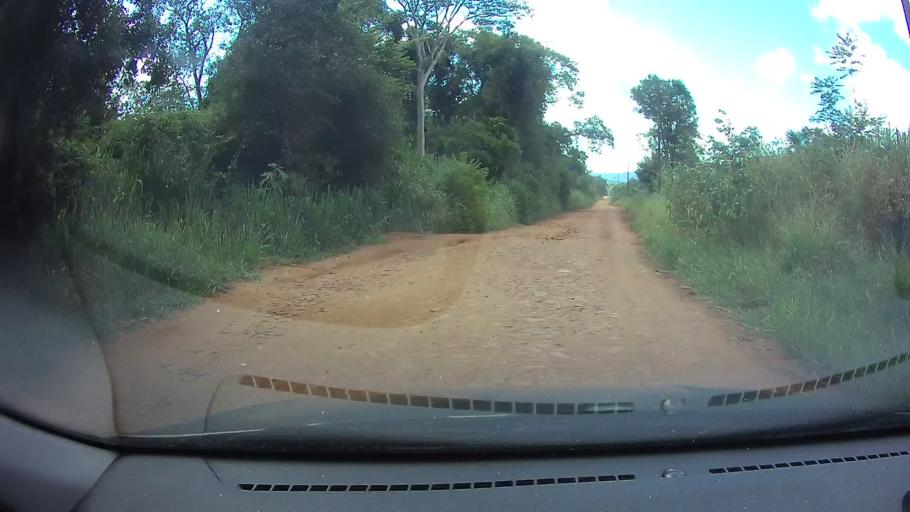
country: PY
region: Paraguari
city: La Colmena
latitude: -25.9249
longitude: -56.7929
